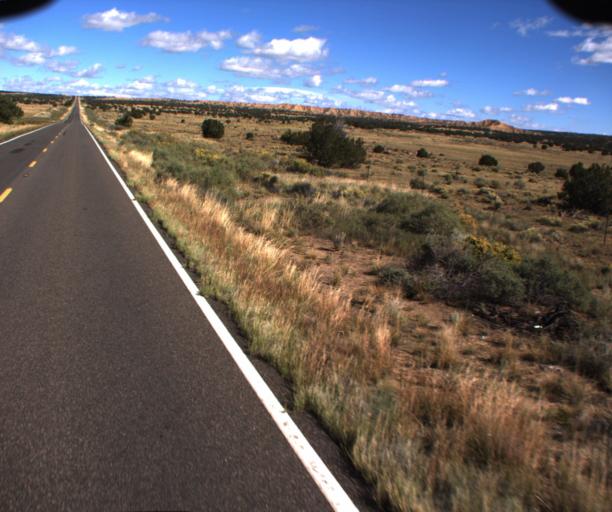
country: US
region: Arizona
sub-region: Apache County
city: Saint Johns
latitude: 34.7934
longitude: -109.2381
